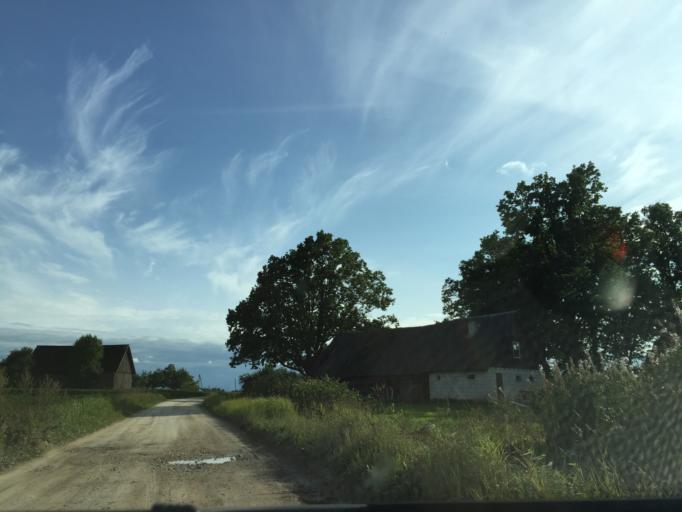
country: LV
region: Kegums
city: Kegums
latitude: 56.8199
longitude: 24.7598
